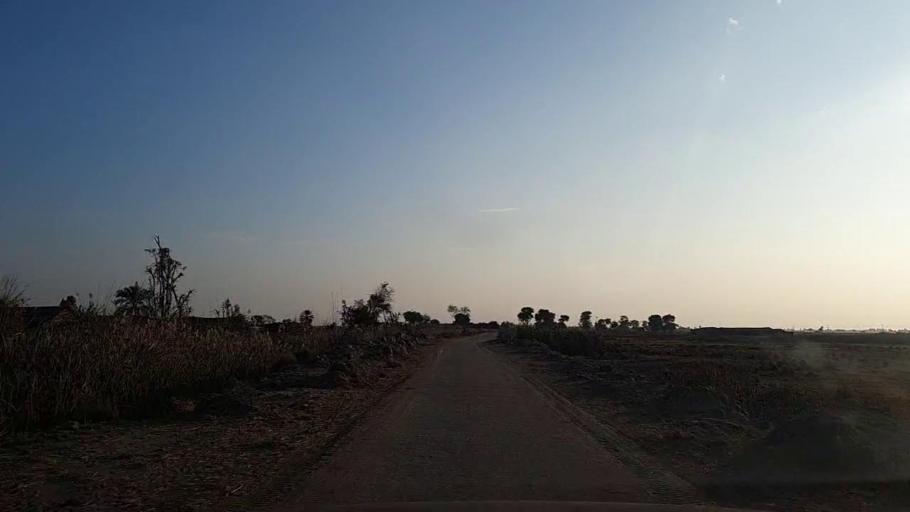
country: PK
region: Sindh
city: Sanghar
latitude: 26.2675
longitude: 68.9817
